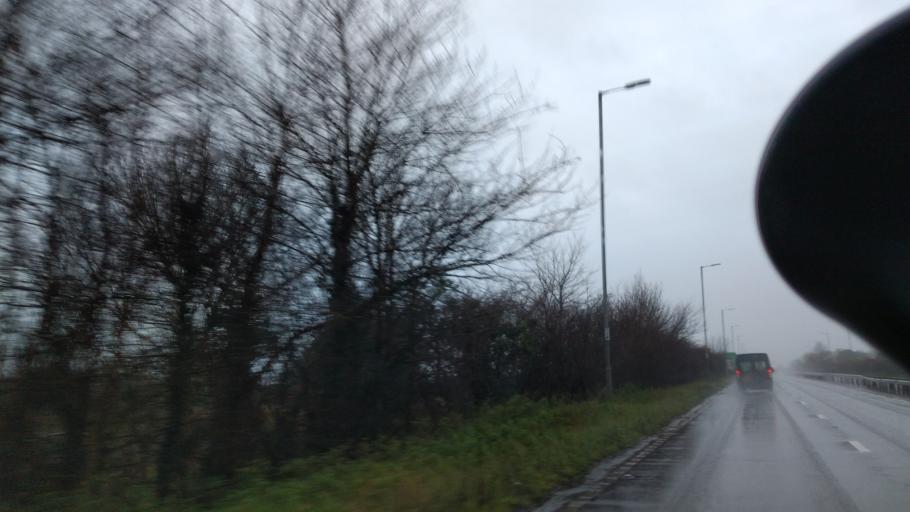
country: GB
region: England
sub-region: West Sussex
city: Lancing
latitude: 50.8374
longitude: -0.3454
